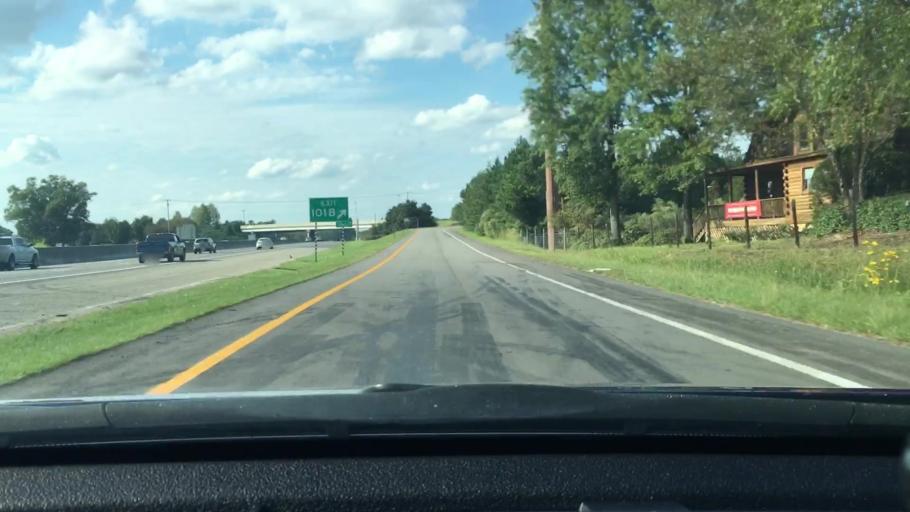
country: US
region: South Carolina
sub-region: Lexington County
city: Irmo
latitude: 34.0964
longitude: -81.1715
